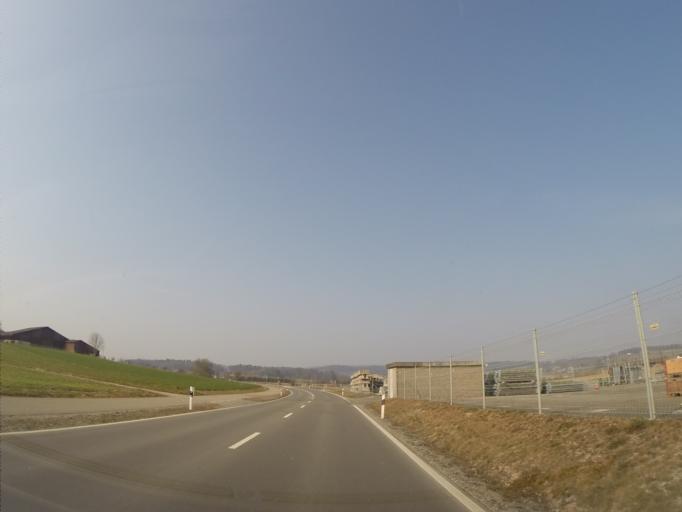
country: CH
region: Zurich
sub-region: Bezirk Andelfingen
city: Kleinandelfingen
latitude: 47.6178
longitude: 8.6832
